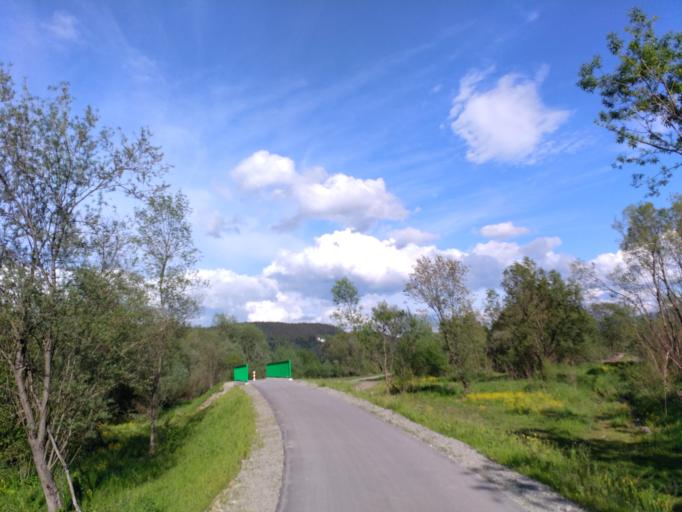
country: PL
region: Lesser Poland Voivodeship
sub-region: Powiat nowosadecki
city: Lacko
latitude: 49.5469
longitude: 20.4565
